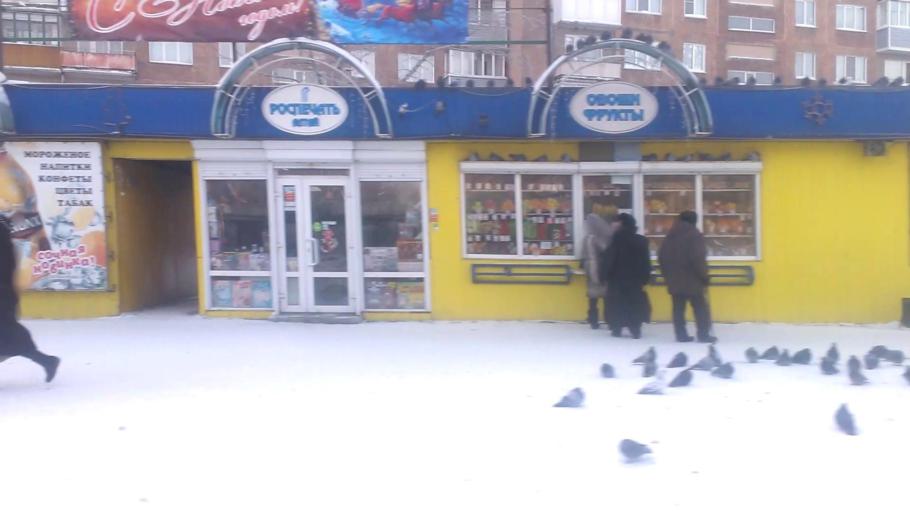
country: RU
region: Altai Krai
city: Novosilikatnyy
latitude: 53.3735
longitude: 83.6684
